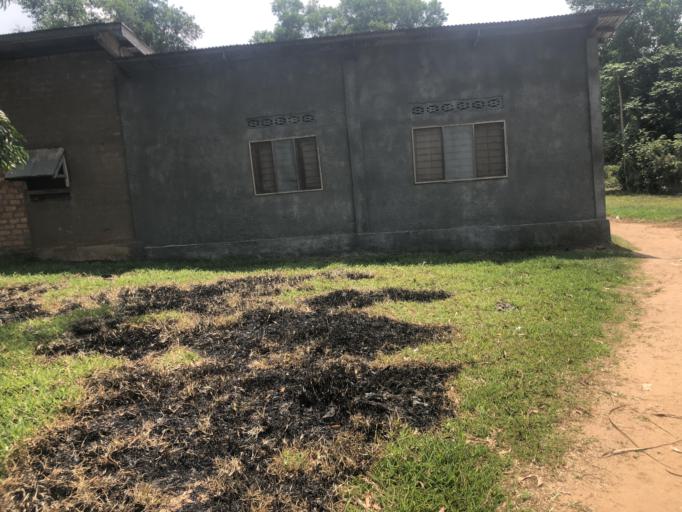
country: CD
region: Bandundu
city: Kikwit
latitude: -5.0712
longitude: 18.8478
